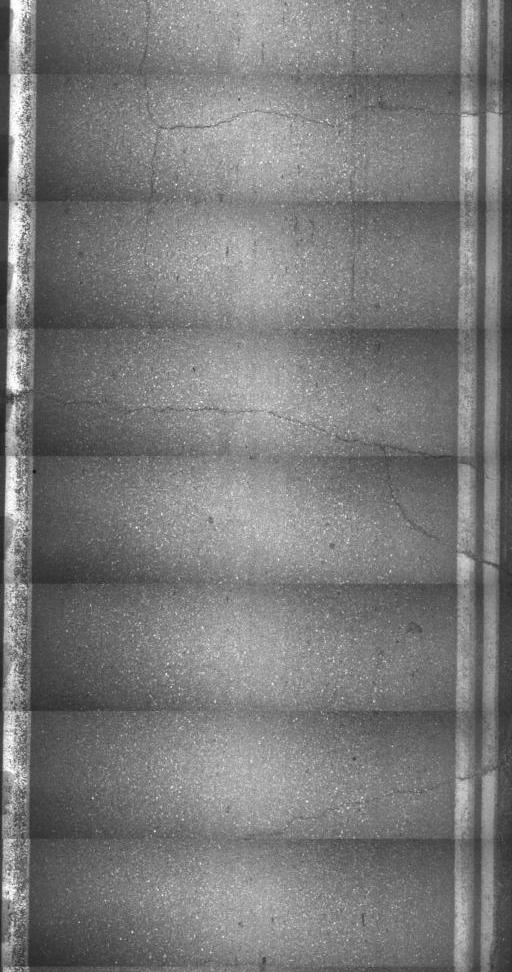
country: US
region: Vermont
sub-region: Caledonia County
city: Saint Johnsbury
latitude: 44.4114
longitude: -71.9321
